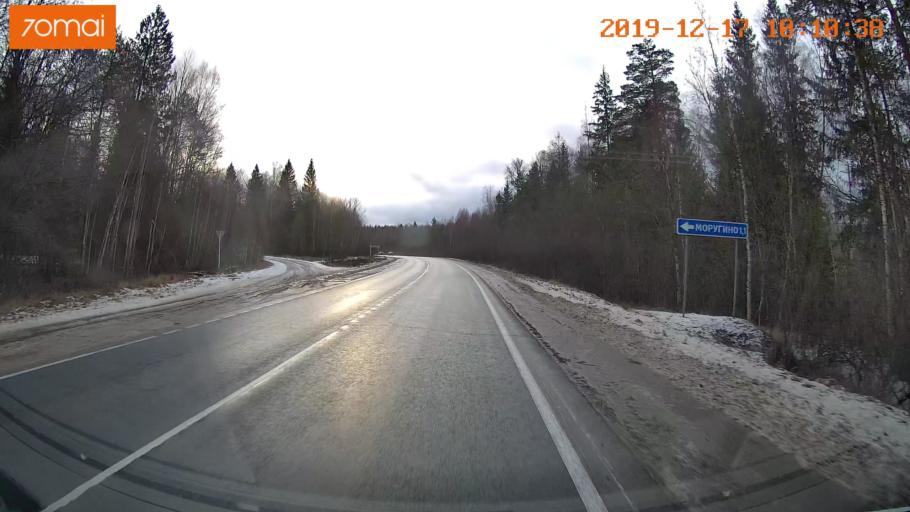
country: RU
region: Vladimir
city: Anopino
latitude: 55.8342
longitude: 40.6439
